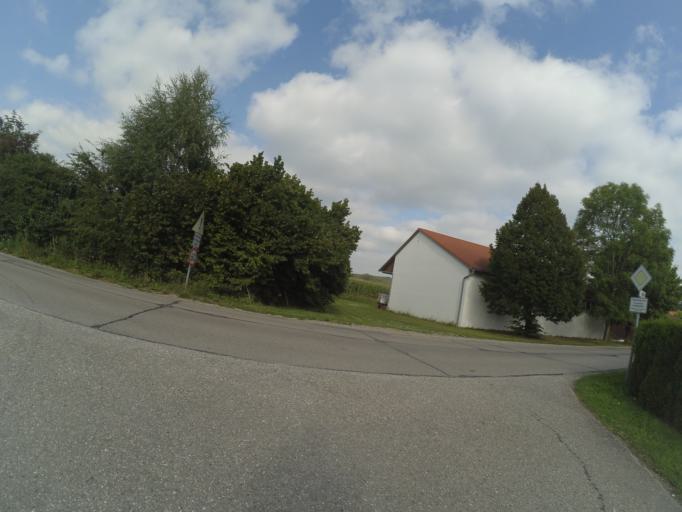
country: DE
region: Bavaria
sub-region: Swabia
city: Waal
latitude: 48.0502
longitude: 10.7830
